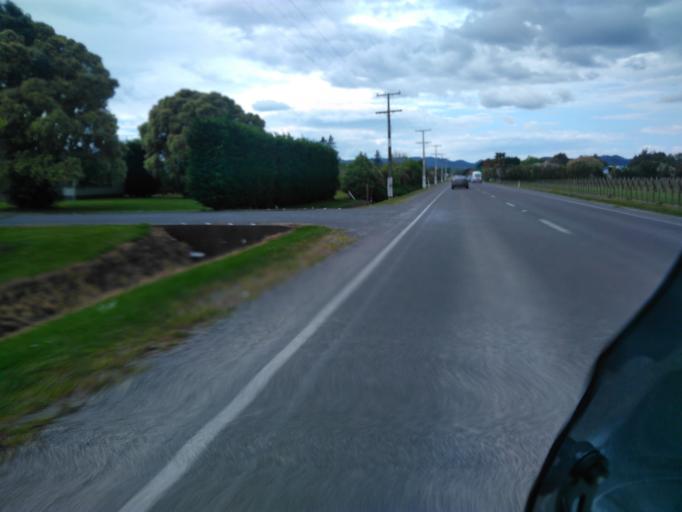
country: NZ
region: Gisborne
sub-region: Gisborne District
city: Gisborne
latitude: -38.6535
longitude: 177.9561
